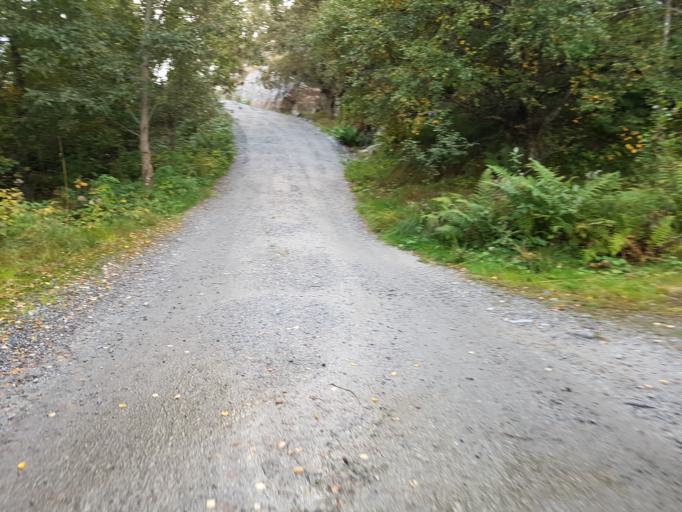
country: NO
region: Sor-Trondelag
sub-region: Afjord
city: A i Afjord
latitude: 64.0561
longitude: 9.9542
